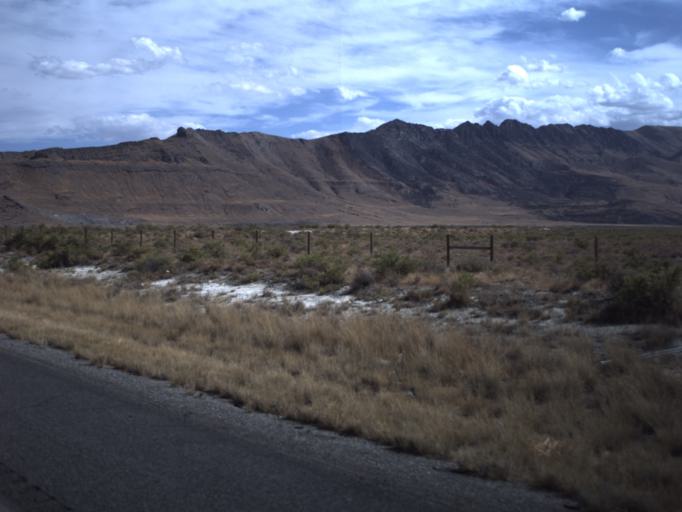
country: US
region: Utah
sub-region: Tooele County
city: Grantsville
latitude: 40.7471
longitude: -112.6683
